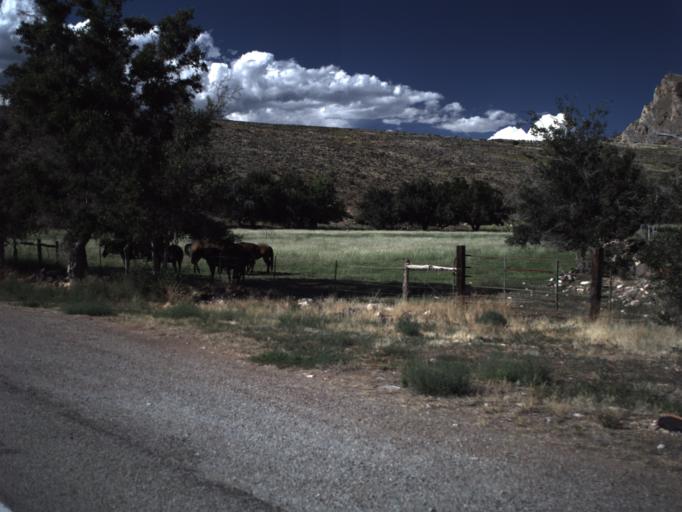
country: US
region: Utah
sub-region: Washington County
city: Toquerville
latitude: 37.2602
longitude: -113.2873
